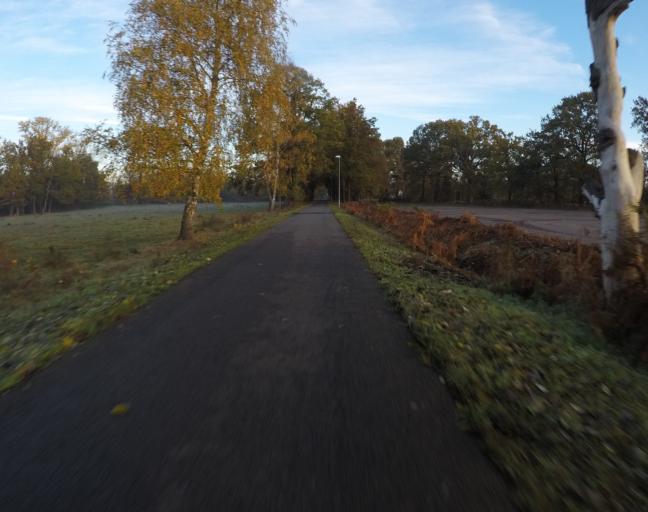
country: BE
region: Flanders
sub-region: Provincie Antwerpen
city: Hulshout
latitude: 51.0496
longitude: 4.8250
